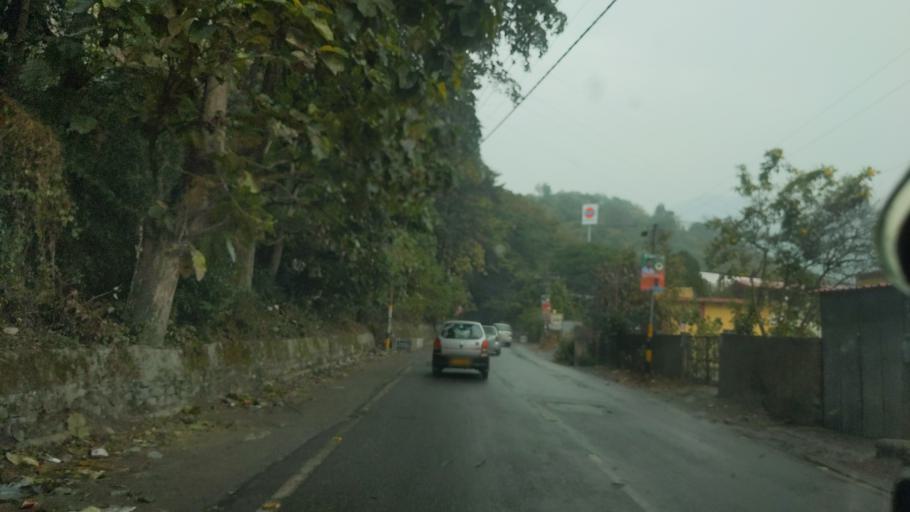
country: IN
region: Uttarakhand
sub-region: Naini Tal
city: Haldwani
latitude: 29.2807
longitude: 79.5451
